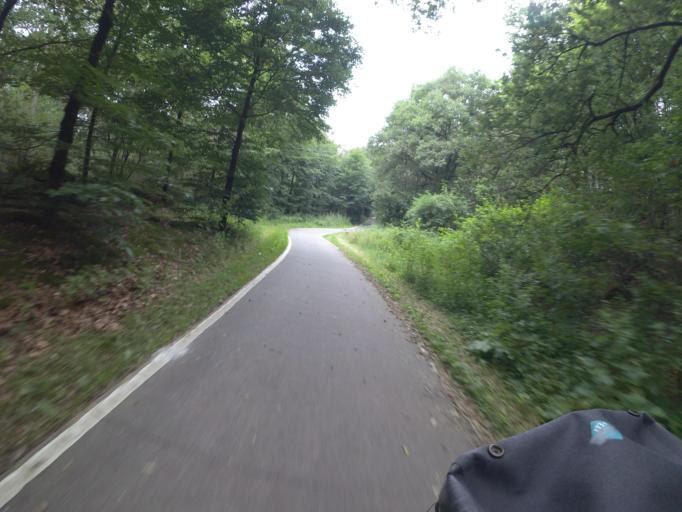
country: NL
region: Gelderland
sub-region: Gemeente Renkum
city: Wolfheze
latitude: 52.0009
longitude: 5.8172
